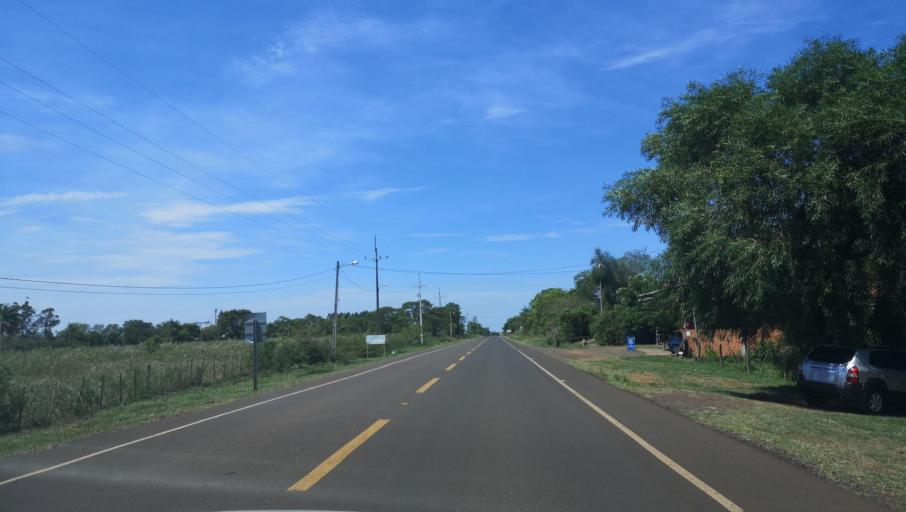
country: PY
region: Misiones
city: Santa Maria
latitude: -26.9065
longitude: -57.0282
